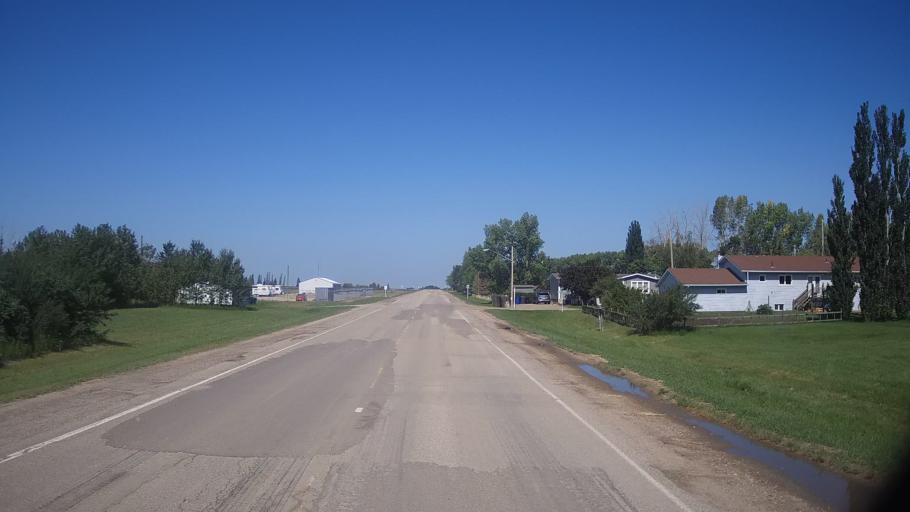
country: CA
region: Saskatchewan
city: Saskatoon
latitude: 51.8942
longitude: -106.0596
